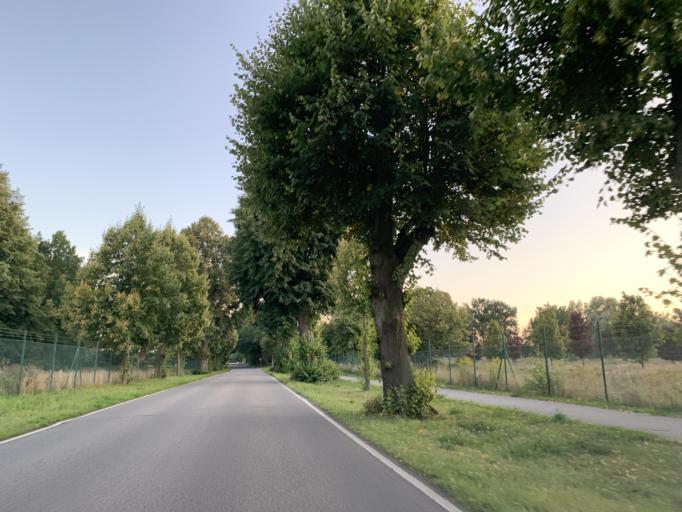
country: DE
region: Mecklenburg-Vorpommern
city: Burg Stargard
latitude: 53.5209
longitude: 13.2836
